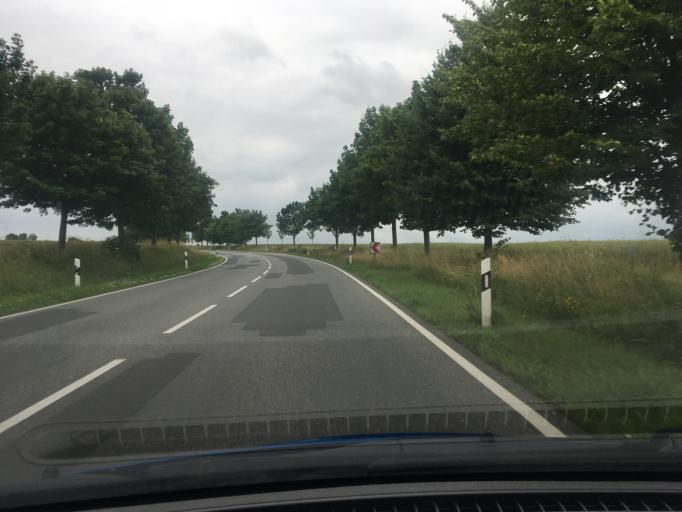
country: DE
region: Mecklenburg-Vorpommern
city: Stralendorf
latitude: 53.5403
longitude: 11.3071
